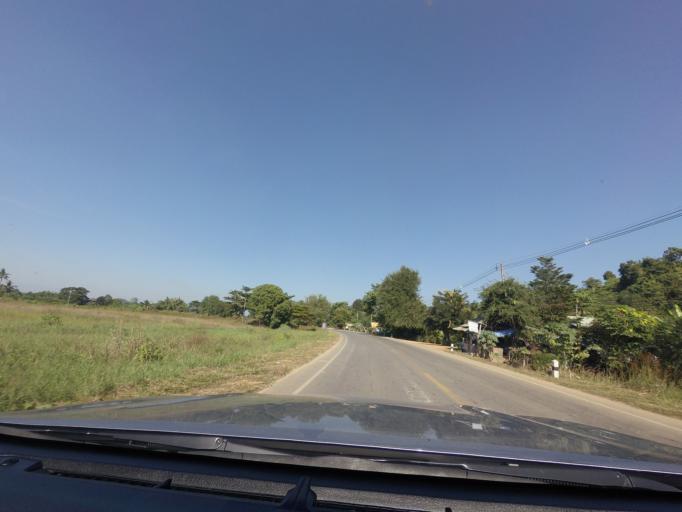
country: TH
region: Sukhothai
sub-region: Amphoe Si Satchanalai
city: Si Satchanalai
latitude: 17.6806
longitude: 99.7044
